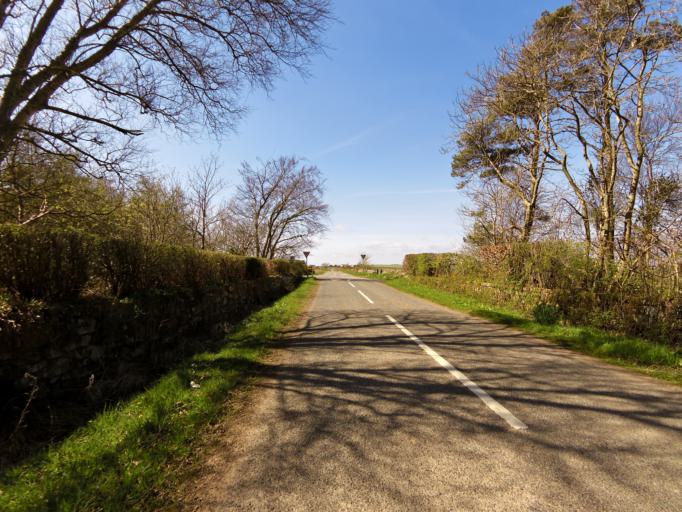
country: GB
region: Scotland
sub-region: Angus
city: Montrose
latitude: 56.6753
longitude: -2.4956
